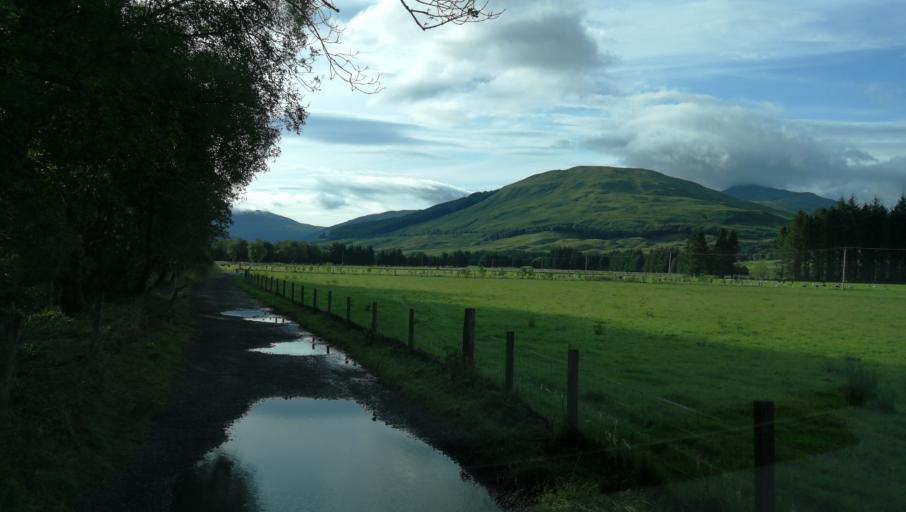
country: GB
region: Scotland
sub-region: Argyll and Bute
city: Garelochhead
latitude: 56.4166
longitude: -4.6631
